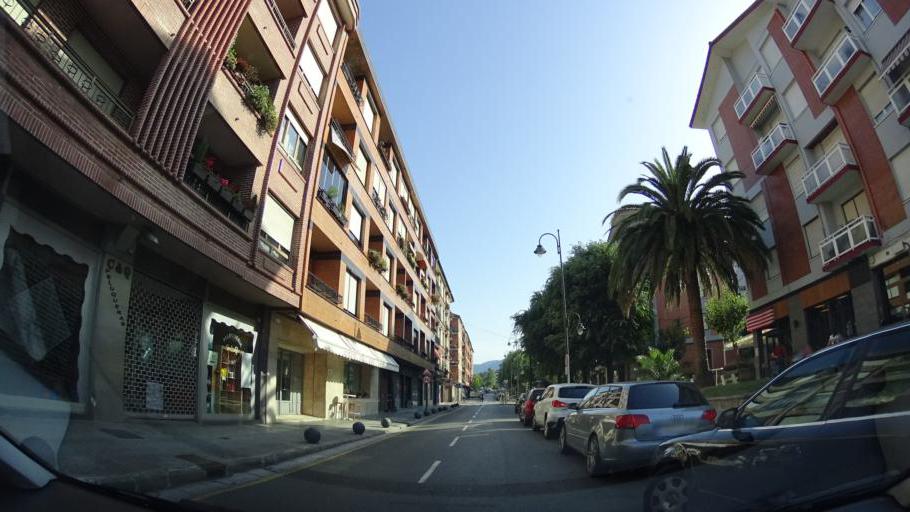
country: ES
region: Basque Country
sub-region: Bizkaia
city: Gernika-Lumo
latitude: 43.3086
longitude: -2.6800
